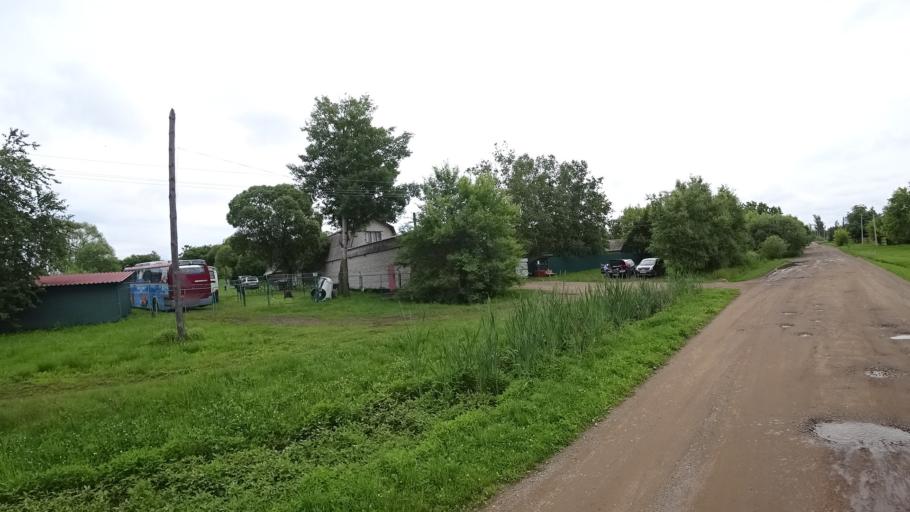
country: RU
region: Primorskiy
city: Novosysoyevka
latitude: 44.2508
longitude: 133.3761
